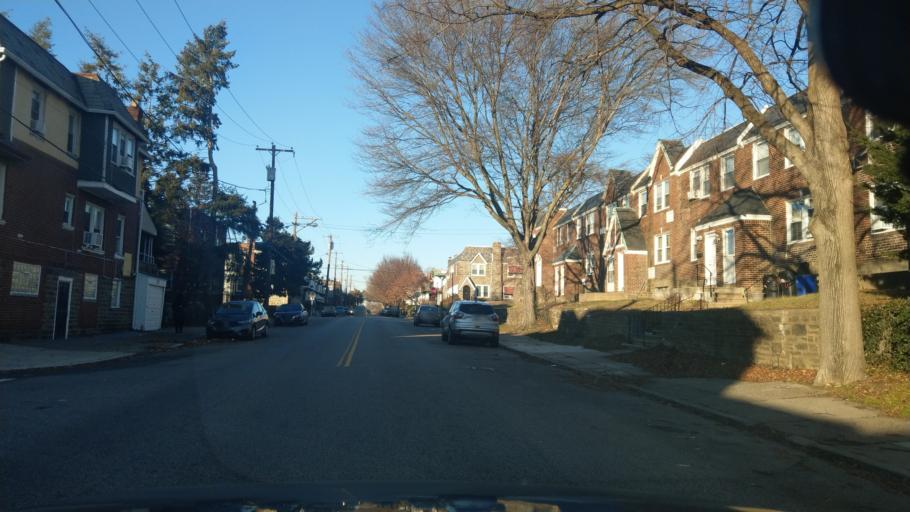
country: US
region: Pennsylvania
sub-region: Montgomery County
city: Wyncote
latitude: 40.0547
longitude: -75.1430
